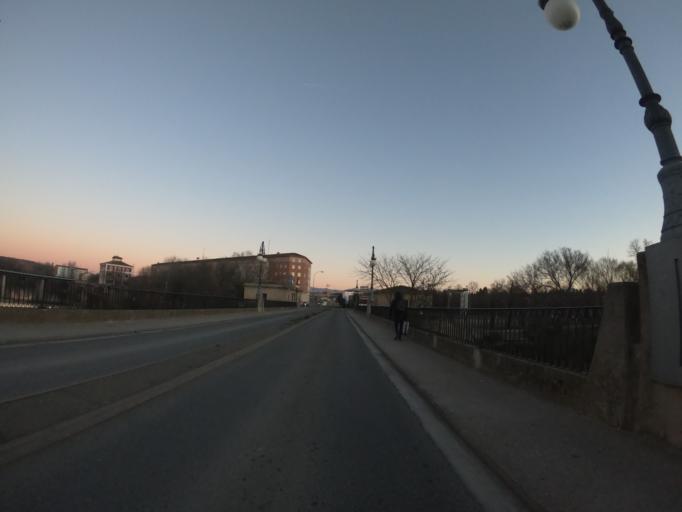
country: ES
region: La Rioja
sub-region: Provincia de La Rioja
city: Logrono
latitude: 42.4703
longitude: -2.4438
